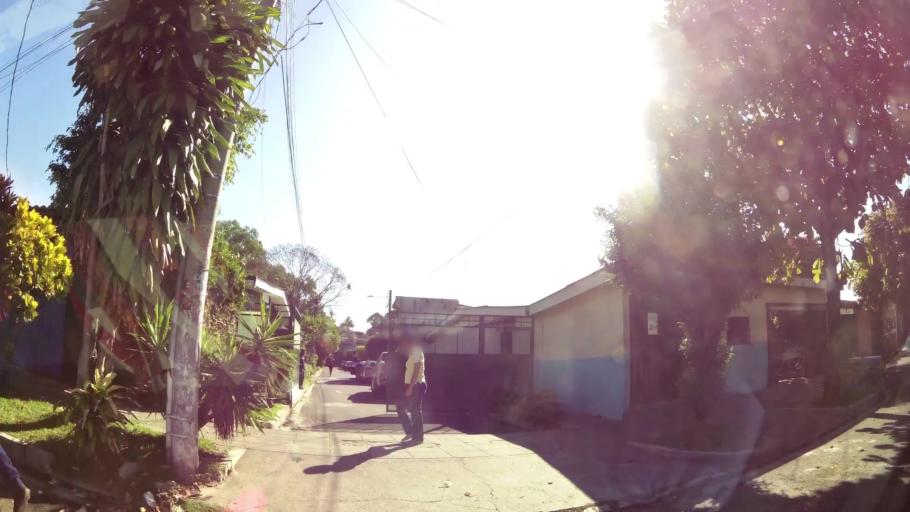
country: SV
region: La Libertad
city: Santa Tecla
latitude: 13.6797
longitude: -89.2923
